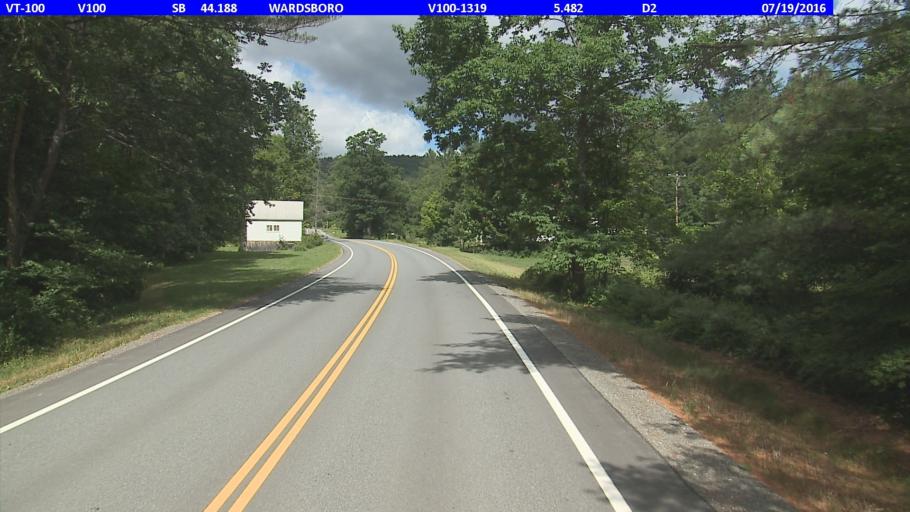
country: US
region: Vermont
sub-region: Windham County
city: Dover
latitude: 43.0775
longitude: -72.8646
